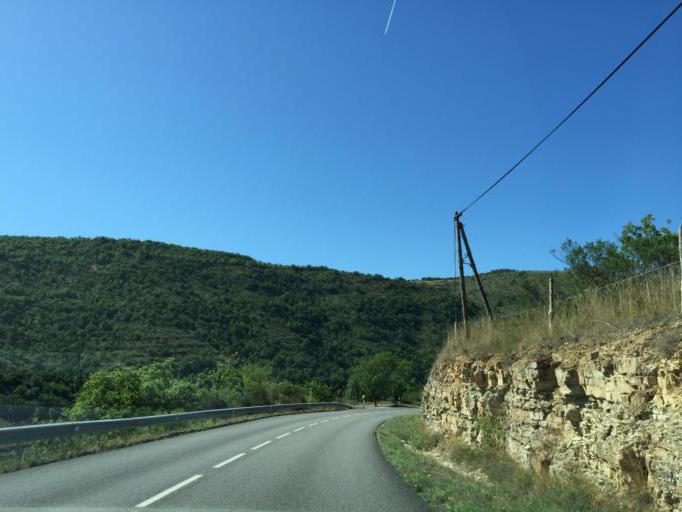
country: FR
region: Midi-Pyrenees
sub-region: Departement de l'Aveyron
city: Saint-Georges-de-Luzencon
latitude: 44.0593
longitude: 2.9149
